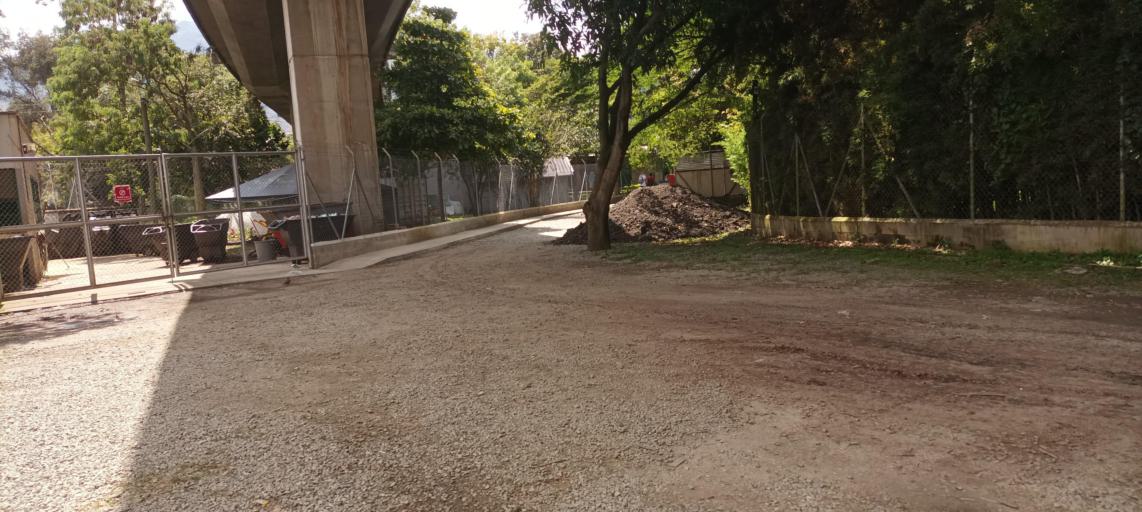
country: CO
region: Antioquia
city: Medellin
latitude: 6.2706
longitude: -75.5689
